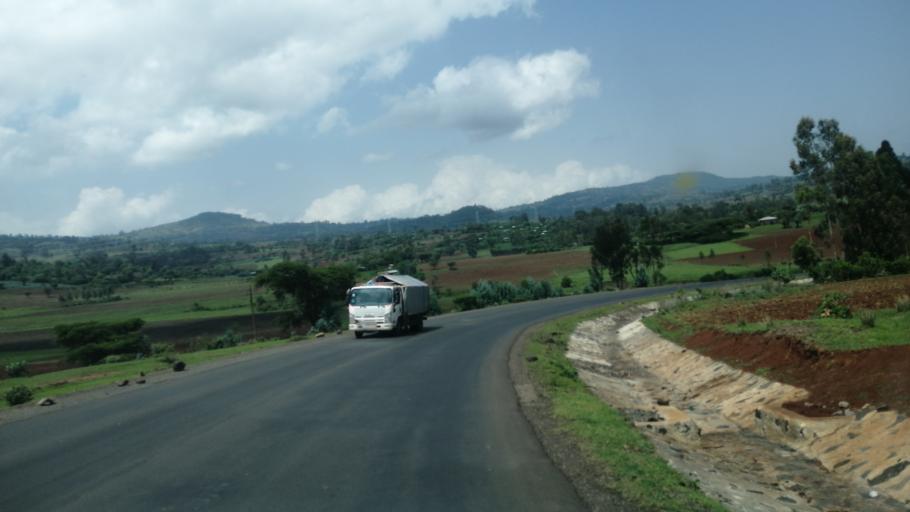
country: ET
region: Oromiya
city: Gedo
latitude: 8.9749
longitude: 37.5590
